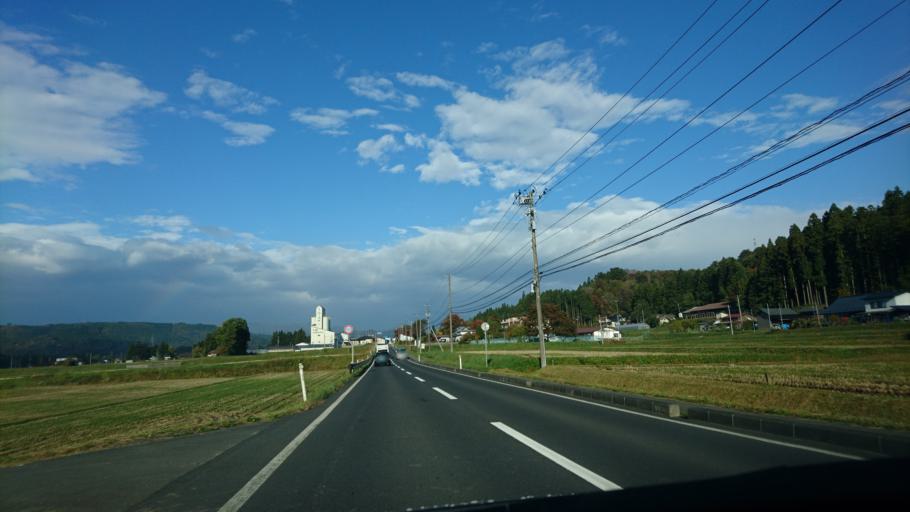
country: JP
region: Iwate
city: Ichinoseki
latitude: 39.0177
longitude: 141.0987
